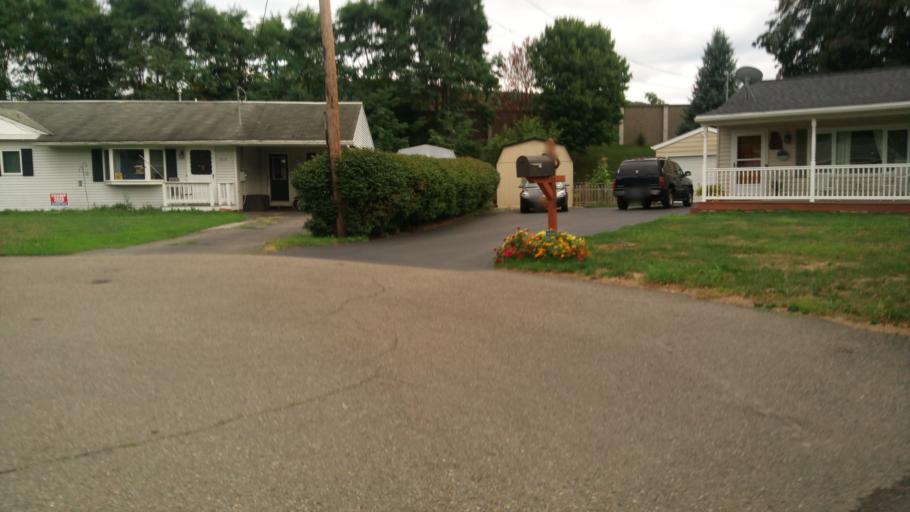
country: US
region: New York
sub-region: Chemung County
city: Southport
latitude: 42.0577
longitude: -76.8131
